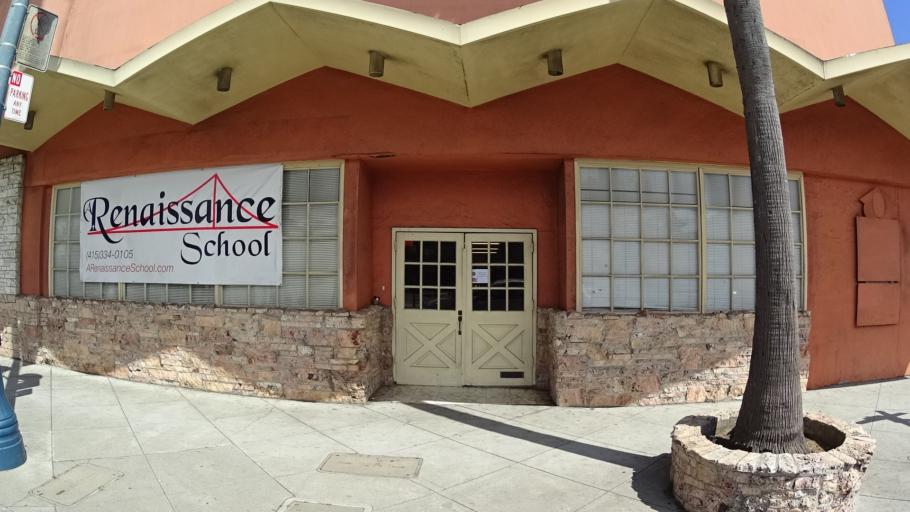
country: US
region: California
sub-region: San Mateo County
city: Daly City
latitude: 37.7260
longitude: -122.4639
